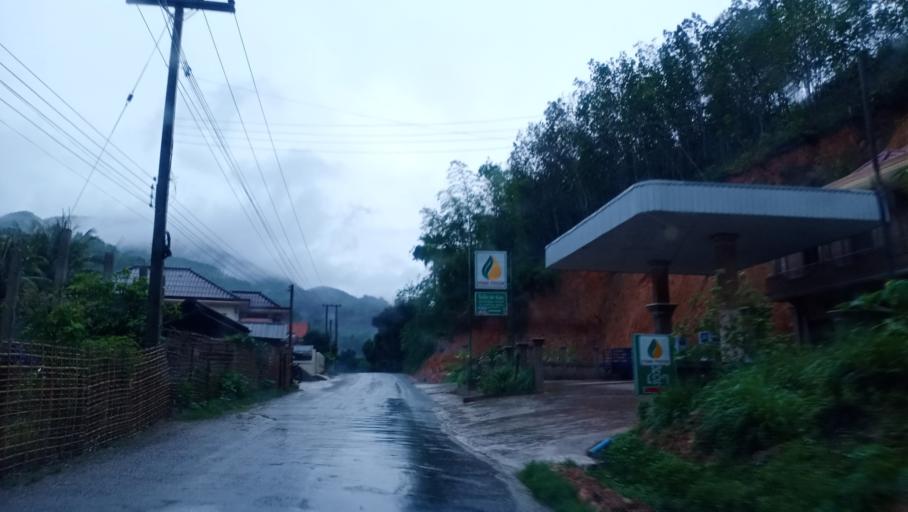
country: LA
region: Phongsali
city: Khoa
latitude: 21.0688
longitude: 102.4906
